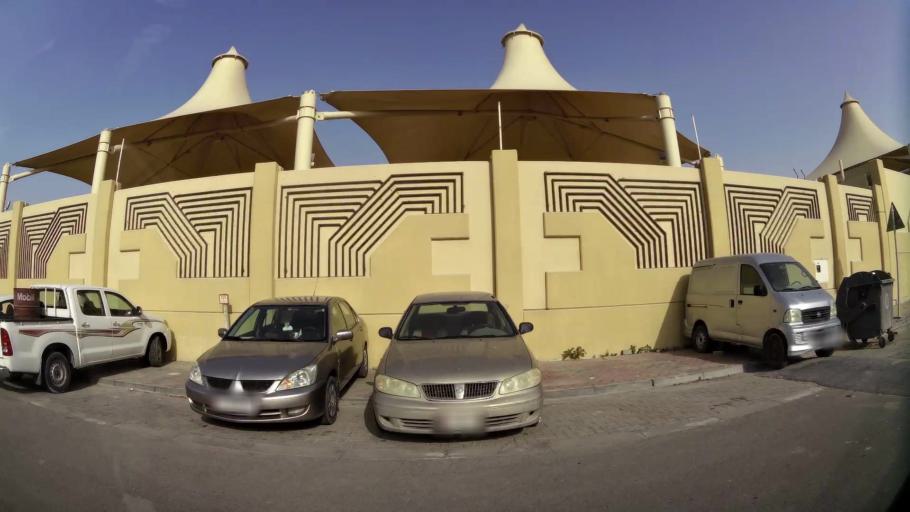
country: QA
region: Baladiyat ar Rayyan
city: Ar Rayyan
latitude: 25.2332
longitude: 51.4329
